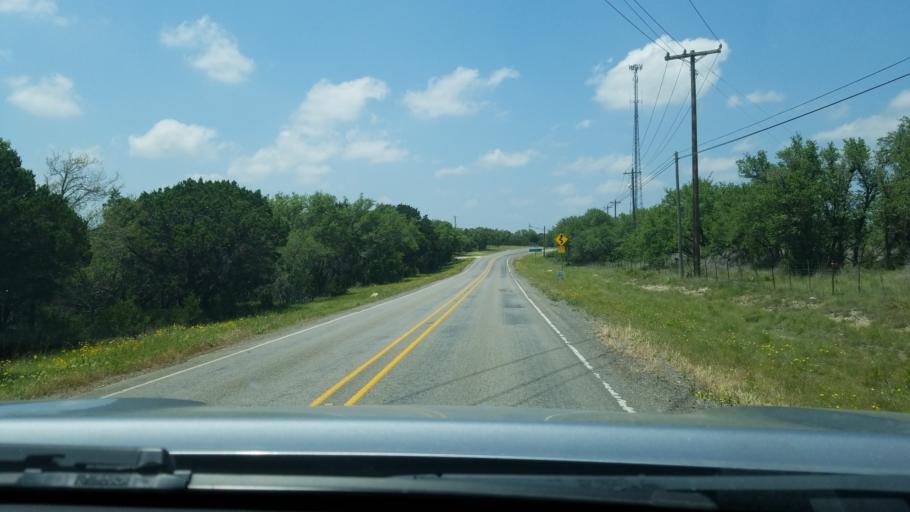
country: US
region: Texas
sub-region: Hays County
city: Woodcreek
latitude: 30.0463
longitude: -98.1970
